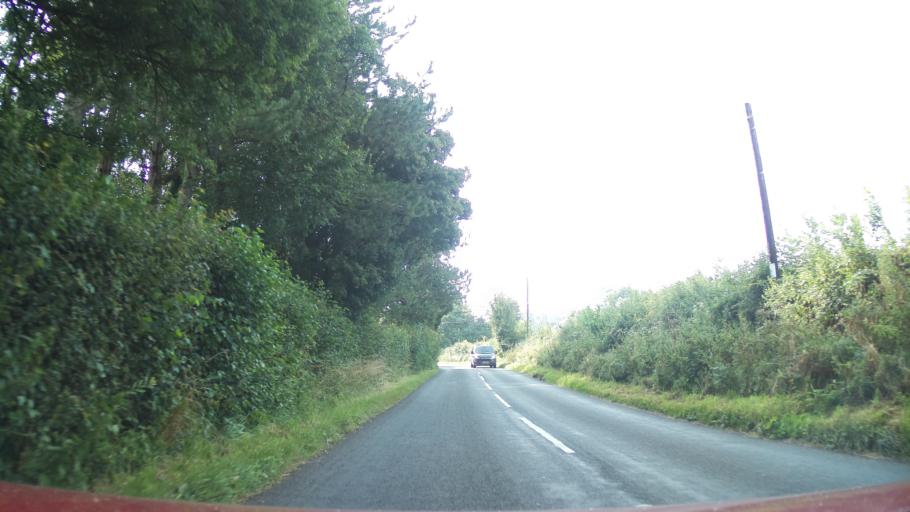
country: GB
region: England
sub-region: Bath and North East Somerset
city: East Harptree
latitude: 51.2913
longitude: -2.5931
